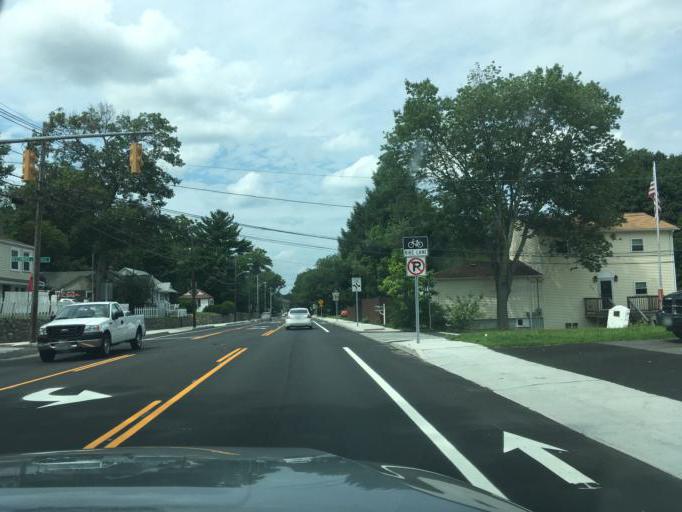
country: US
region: Rhode Island
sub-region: Kent County
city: West Warwick
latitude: 41.6742
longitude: -71.5546
